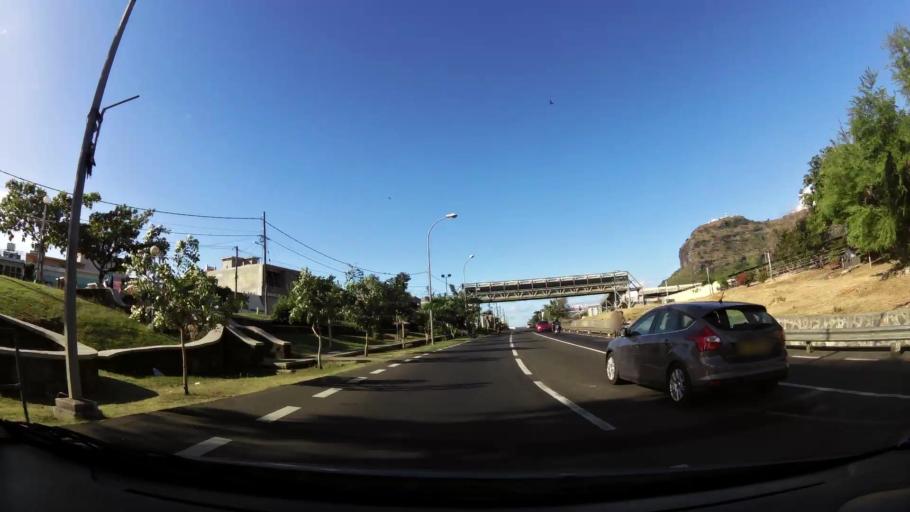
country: MU
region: Port Louis
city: Port Louis
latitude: -20.1712
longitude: 57.4781
